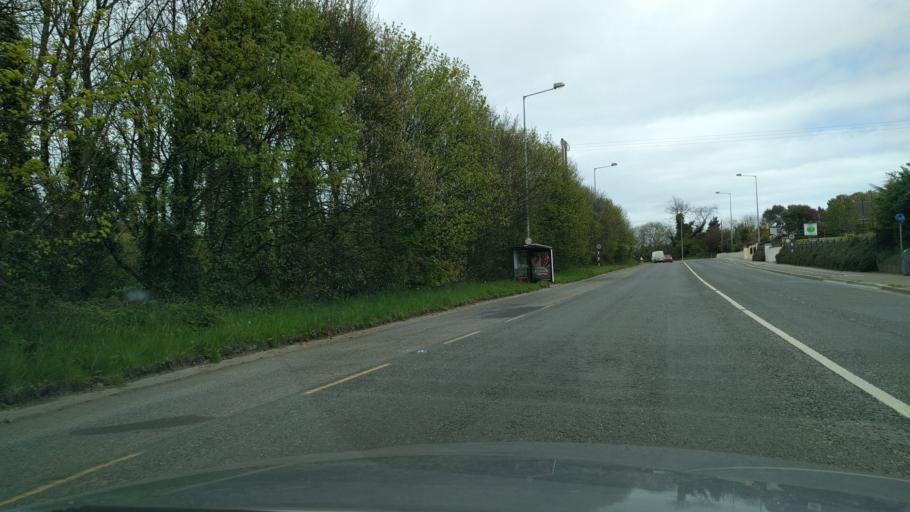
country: IE
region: Leinster
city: Balrothery
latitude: 53.5931
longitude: -6.1860
